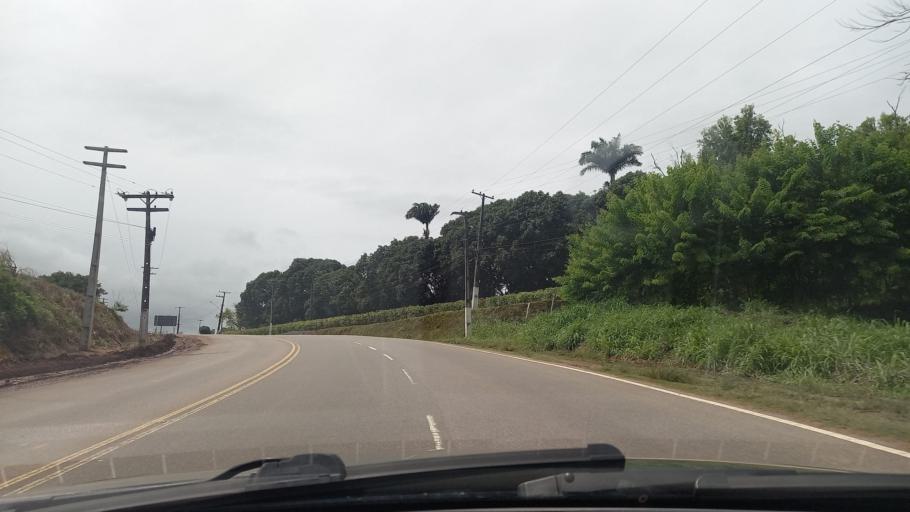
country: BR
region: Alagoas
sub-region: Sao Miguel Dos Campos
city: Sao Miguel dos Campos
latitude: -9.8091
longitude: -36.2124
